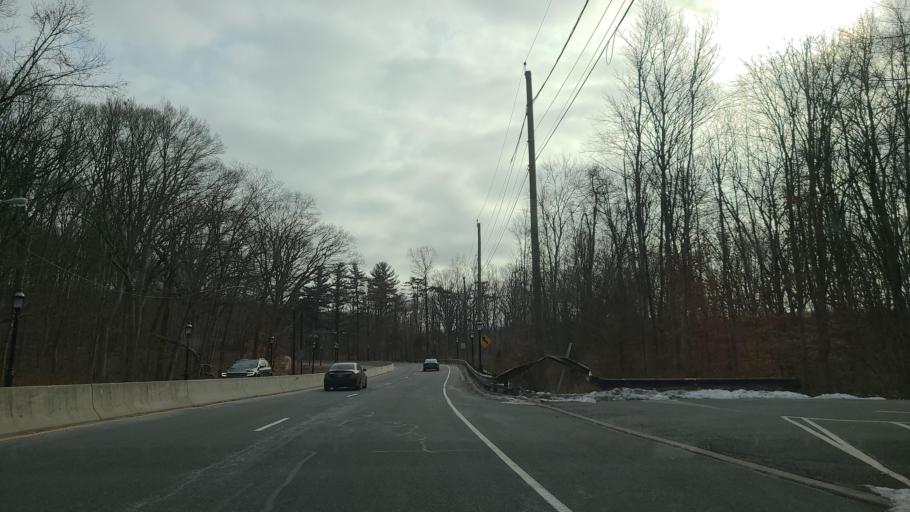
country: US
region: New Jersey
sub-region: Essex County
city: Maplewood
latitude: 40.7533
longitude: -74.2899
